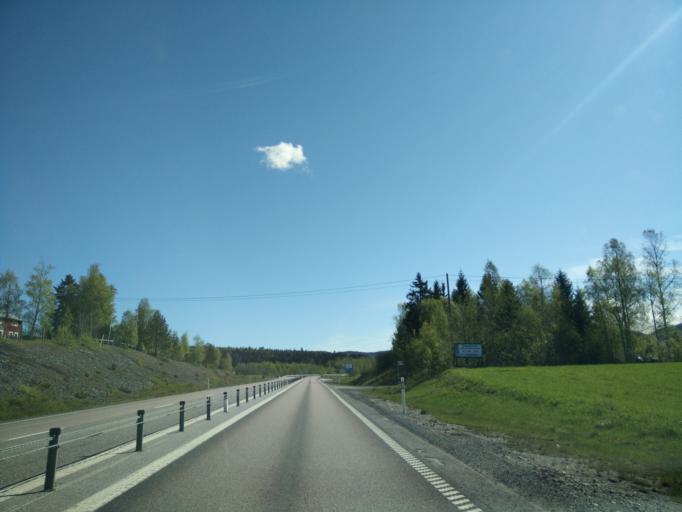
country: SE
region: Vaesternorrland
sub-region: Kramfors Kommun
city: Nordingra
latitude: 62.9586
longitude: 18.1159
